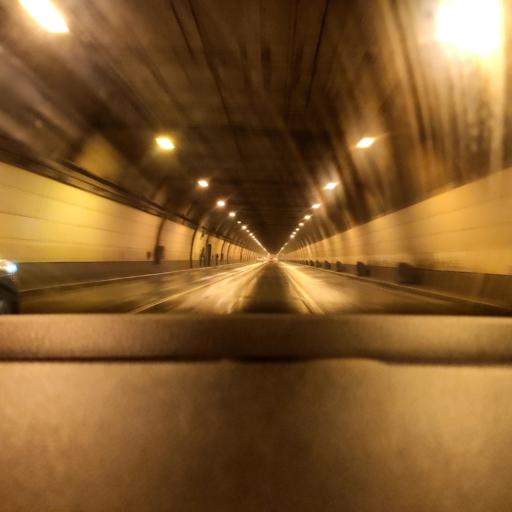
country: RU
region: Moscow
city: Rublevo
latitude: 55.7829
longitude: 37.3928
